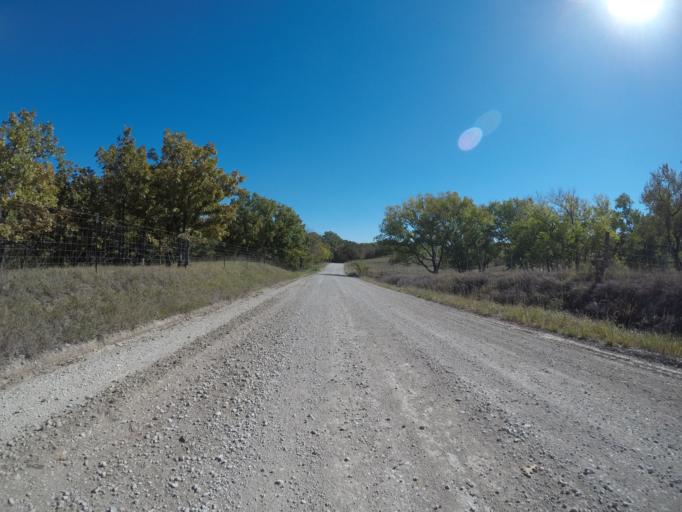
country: US
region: Kansas
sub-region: Wabaunsee County
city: Alma
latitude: 39.0123
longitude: -96.3773
